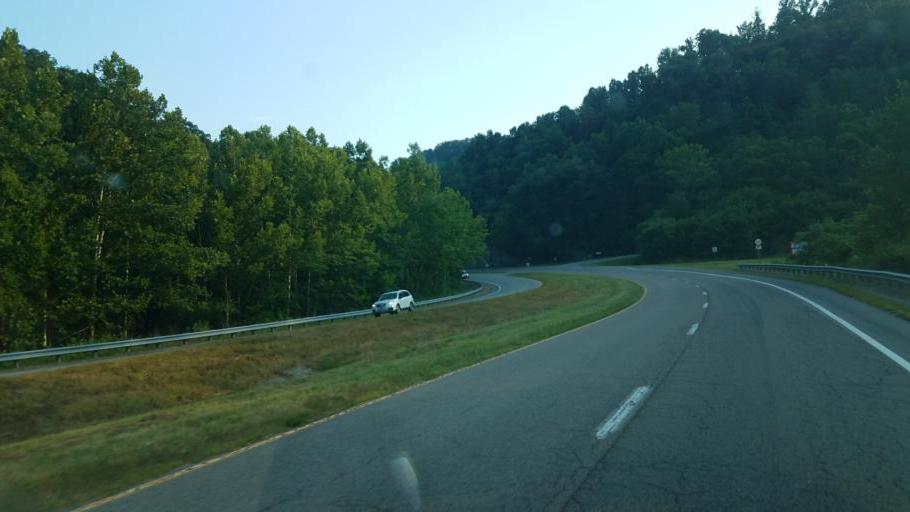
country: US
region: Tennessee
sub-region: Hawkins County
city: Church Hill
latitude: 36.6843
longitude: -82.7543
